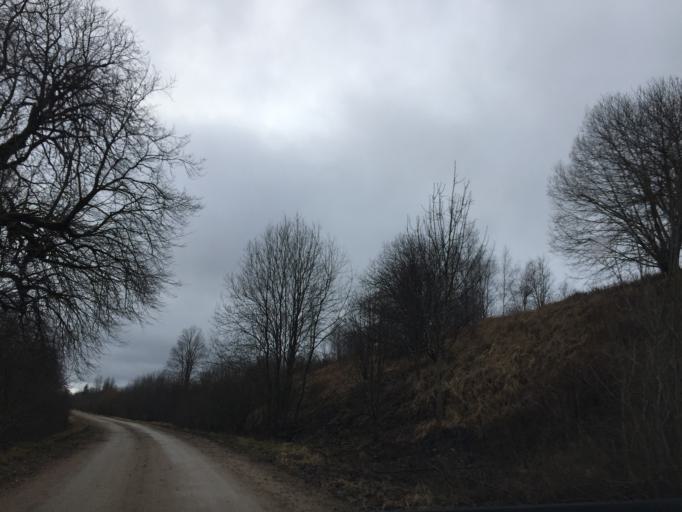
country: LV
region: Broceni
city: Broceni
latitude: 56.6707
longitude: 22.5562
